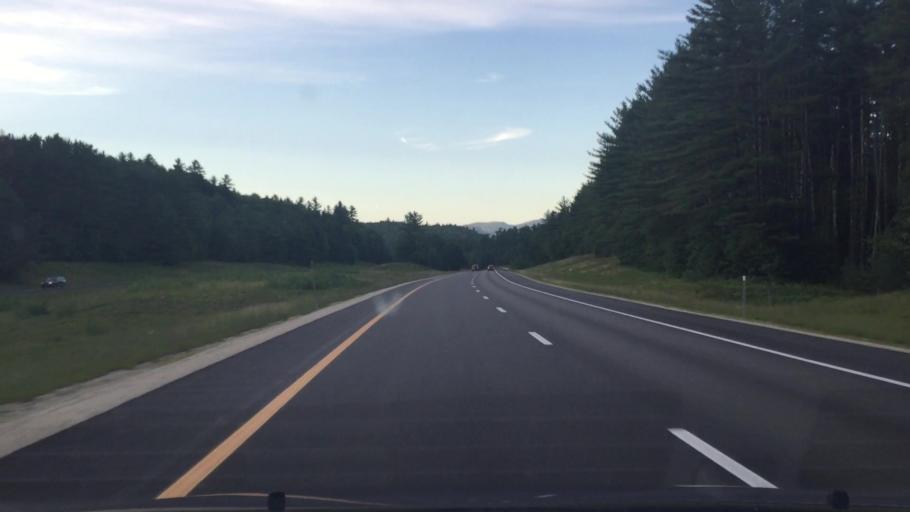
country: US
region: New Hampshire
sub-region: Grafton County
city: Thornton
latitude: 43.9245
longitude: -71.6893
